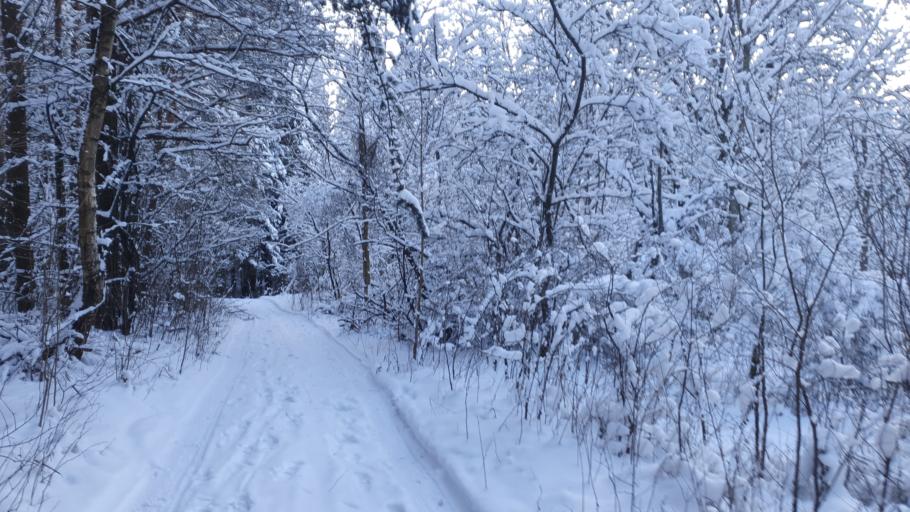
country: LT
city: Skaidiskes
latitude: 54.6423
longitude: 25.4166
